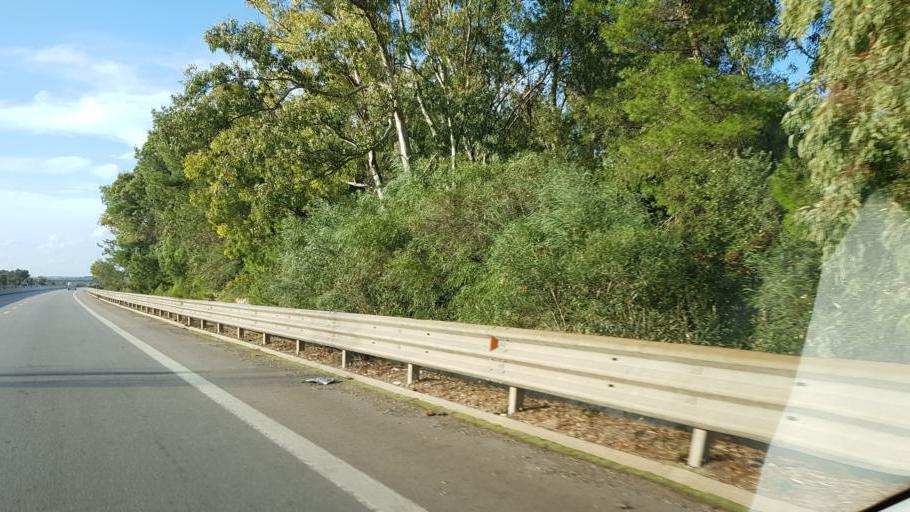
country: IT
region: Apulia
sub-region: Provincia di Brindisi
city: Francavilla Fontana
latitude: 40.5372
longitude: 17.6100
